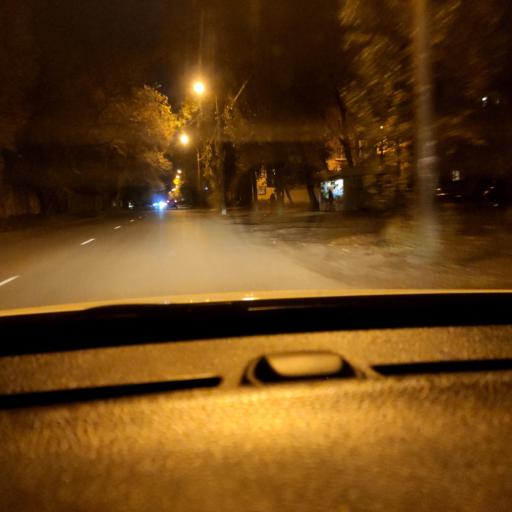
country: RU
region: Voronezj
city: Maslovka
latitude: 51.6096
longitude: 39.2387
